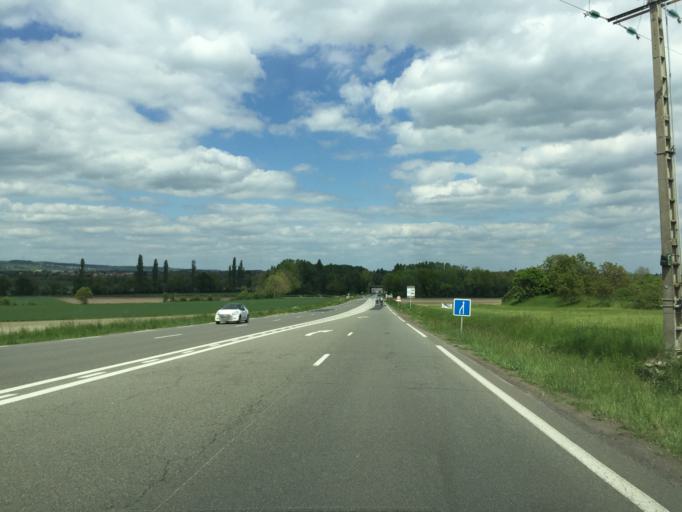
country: FR
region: Auvergne
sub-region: Departement du Puy-de-Dome
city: Saint-Bonnet-pres-Riom
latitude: 45.9426
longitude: 3.1551
